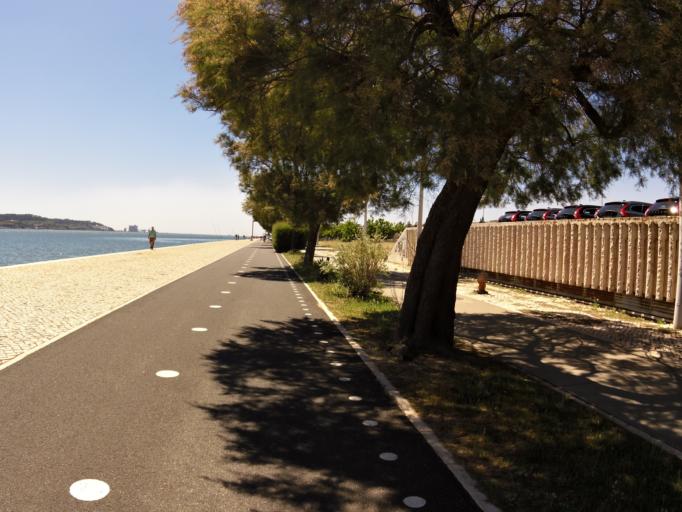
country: PT
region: Setubal
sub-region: Almada
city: Pragal
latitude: 38.6981
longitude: -9.1807
